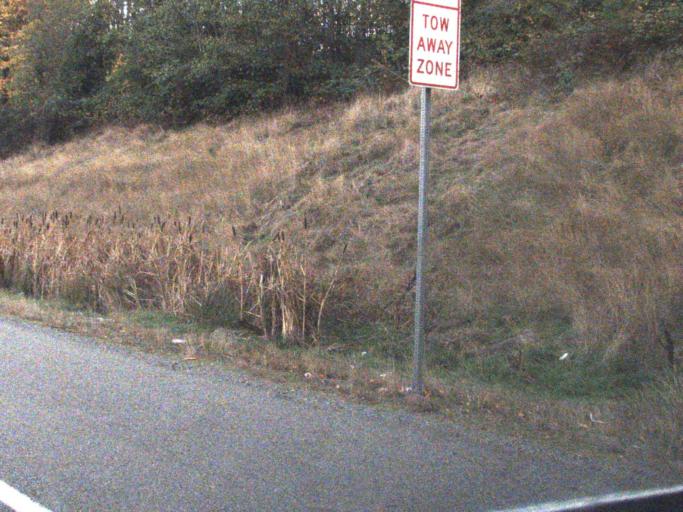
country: US
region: Washington
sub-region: Snohomish County
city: Alderwood Manor
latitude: 47.8487
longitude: -122.2744
